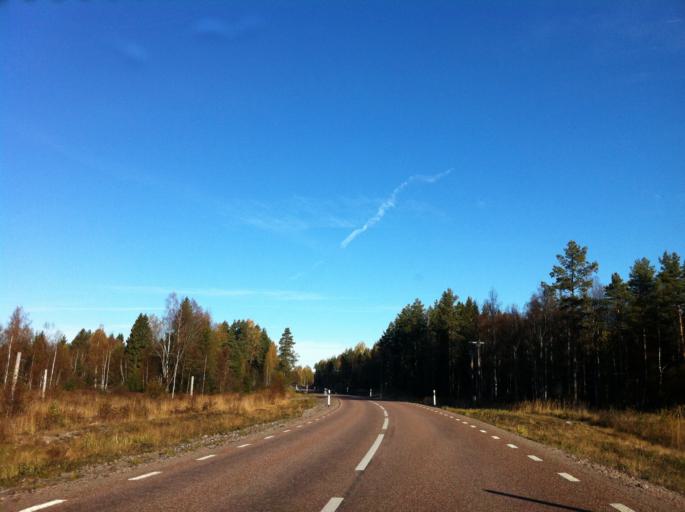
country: SE
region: Gaevleborg
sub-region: Gavle Kommun
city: Gavle
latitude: 60.5677
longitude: 17.1305
